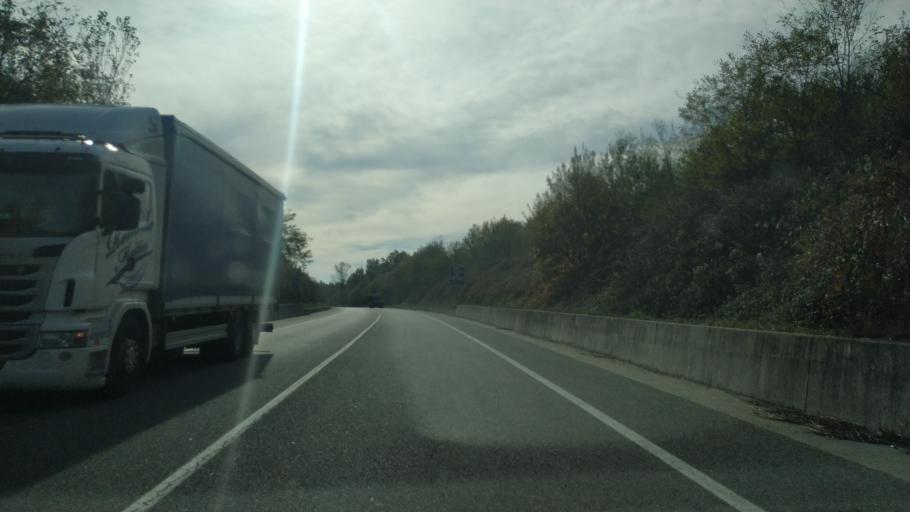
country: IT
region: Piedmont
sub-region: Provincia di Novara
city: Prato Sesia
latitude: 45.6493
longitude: 8.3857
